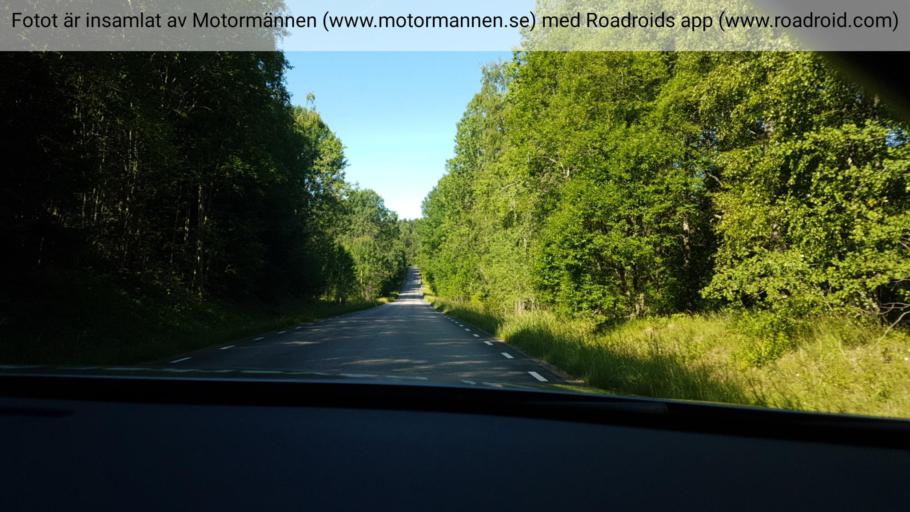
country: SE
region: Vaestra Goetaland
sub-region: Ulricehamns Kommun
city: Ulricehamn
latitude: 57.8298
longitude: 13.2985
